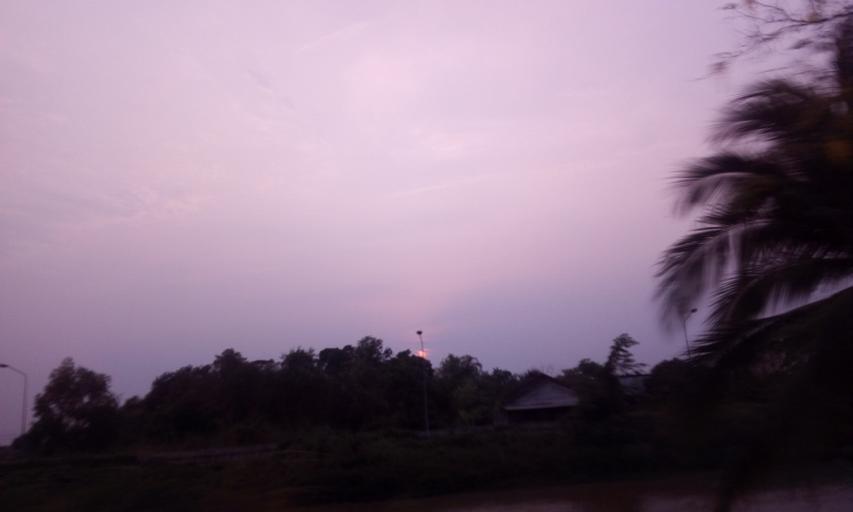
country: TH
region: Pathum Thani
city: Nong Suea
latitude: 14.0599
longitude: 100.8930
